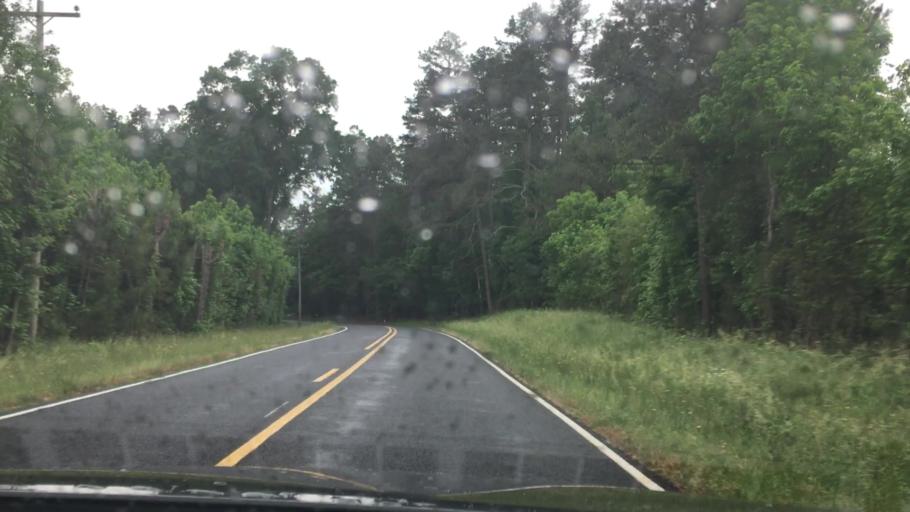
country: US
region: North Carolina
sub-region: Stanly County
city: Badin
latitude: 35.3609
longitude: -80.1168
